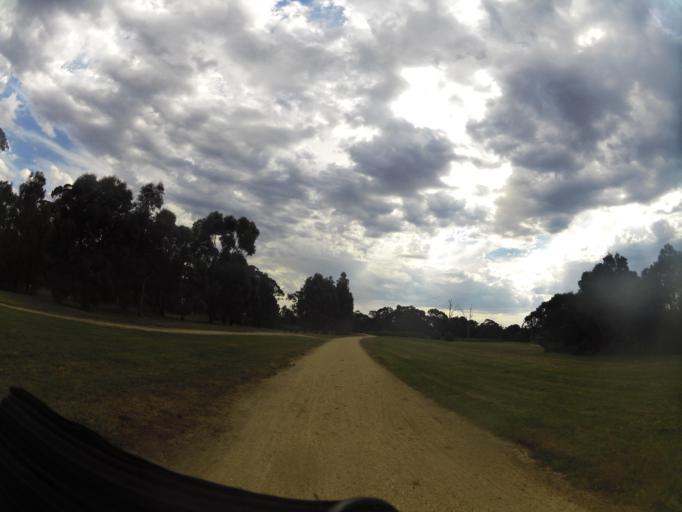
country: AU
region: Victoria
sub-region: Latrobe
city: Traralgon
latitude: -38.0621
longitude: 146.6232
